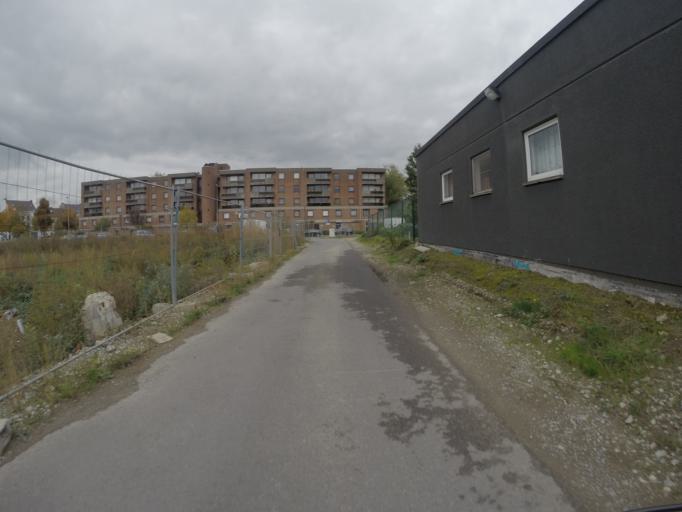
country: BE
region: Flanders
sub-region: Provincie Oost-Vlaanderen
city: Gent
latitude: 51.0654
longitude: 3.7237
